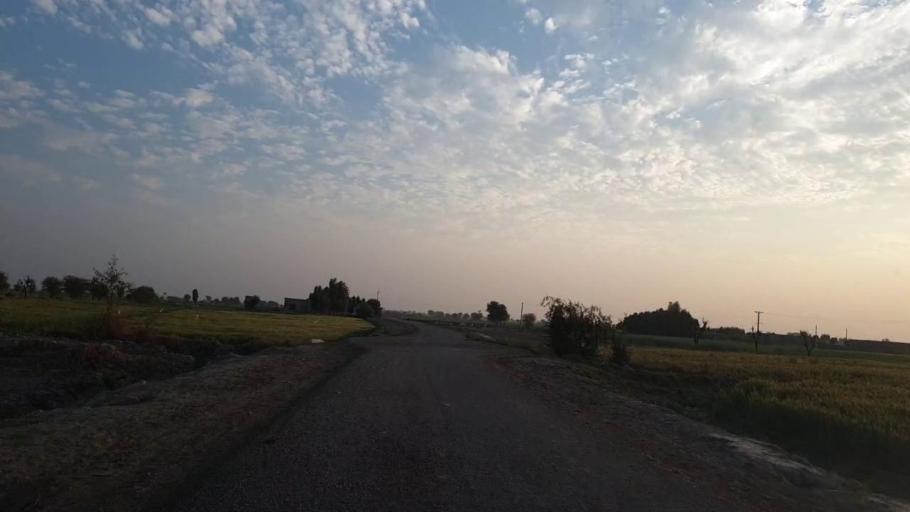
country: PK
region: Sindh
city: Pithoro
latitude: 25.5880
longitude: 69.3046
